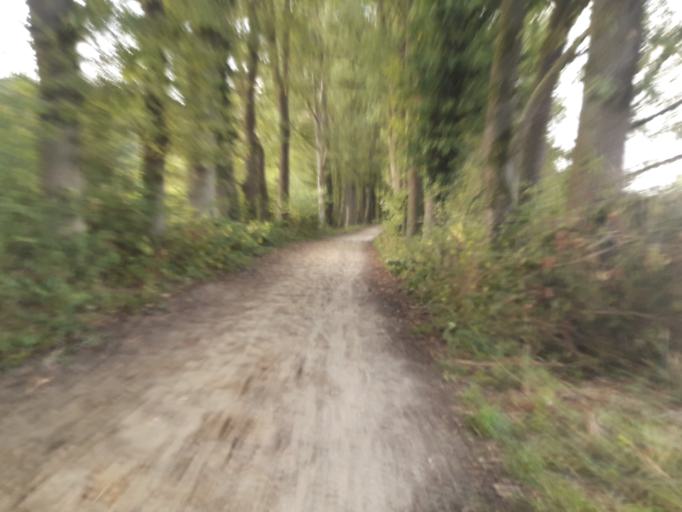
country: DE
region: North Rhine-Westphalia
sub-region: Regierungsbezirk Munster
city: Muenster
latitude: 51.9138
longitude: 7.6701
